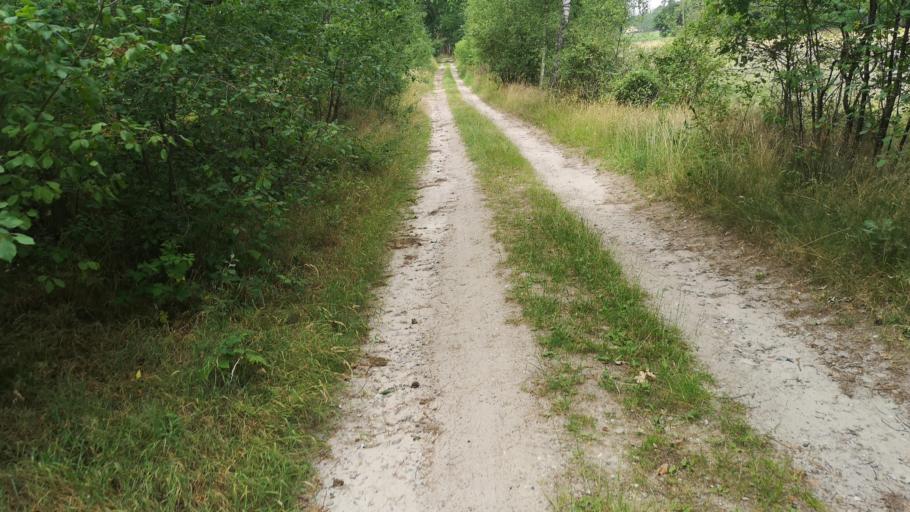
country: DE
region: Lower Saxony
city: Dahlem
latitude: 53.2184
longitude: 10.7365
